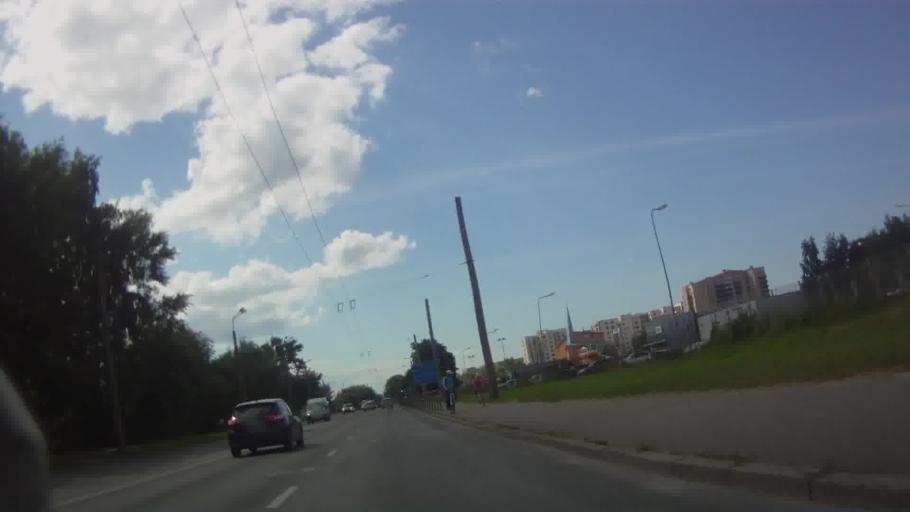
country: LV
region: Riga
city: Riga
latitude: 56.9486
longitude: 24.1904
